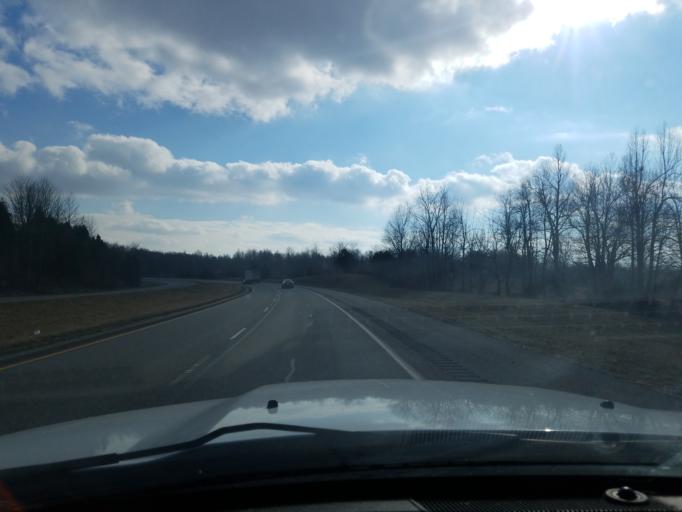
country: US
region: Kentucky
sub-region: Hardin County
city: Elizabethtown
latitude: 37.6444
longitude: -85.8383
